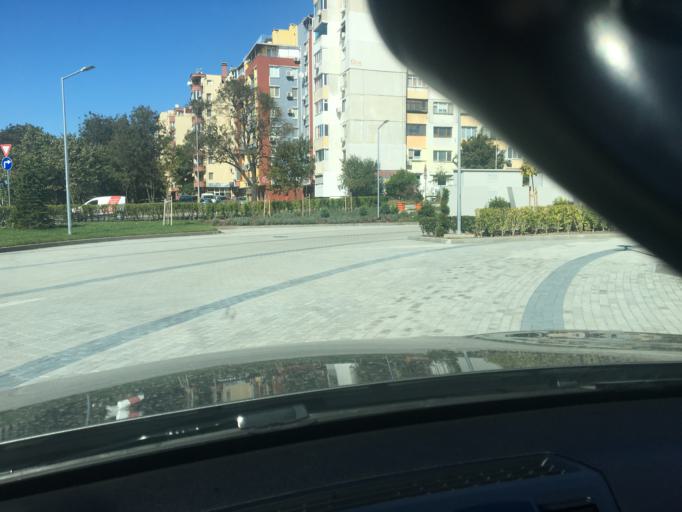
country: BG
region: Burgas
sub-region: Obshtina Burgas
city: Burgas
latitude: 42.5124
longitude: 27.4581
